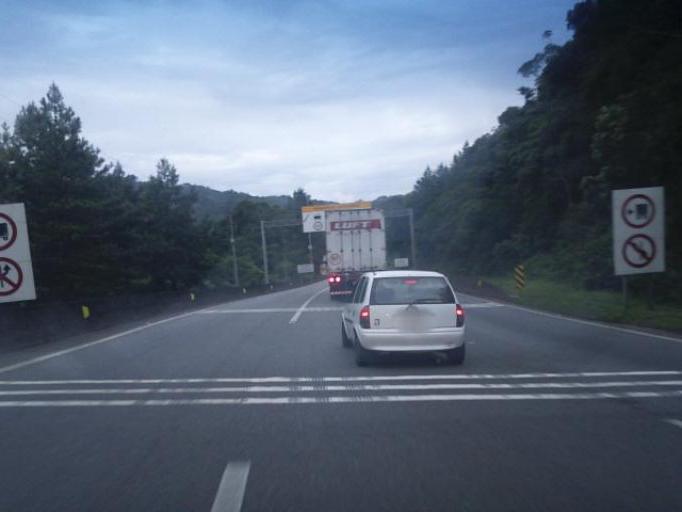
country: BR
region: Parana
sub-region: Guaratuba
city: Guaratuba
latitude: -25.8544
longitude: -48.9570
